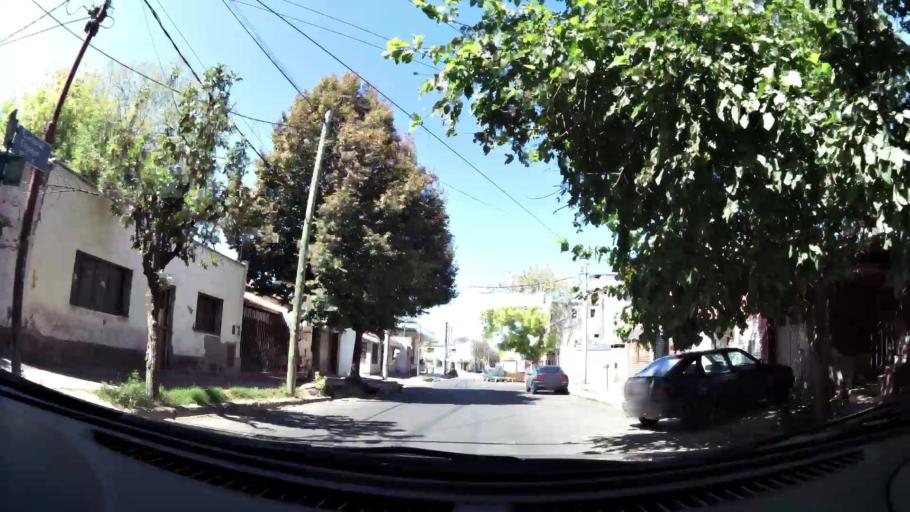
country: AR
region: Mendoza
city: Las Heras
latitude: -32.8527
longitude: -68.8353
